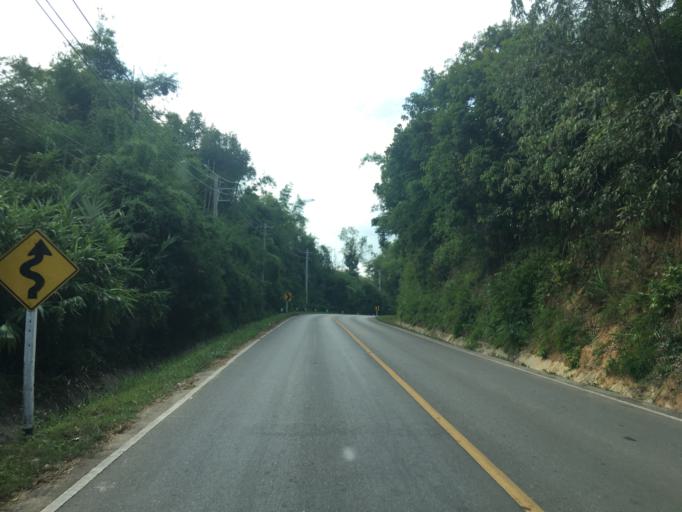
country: TH
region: Nan
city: Ban Luang
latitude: 18.8748
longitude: 100.5908
